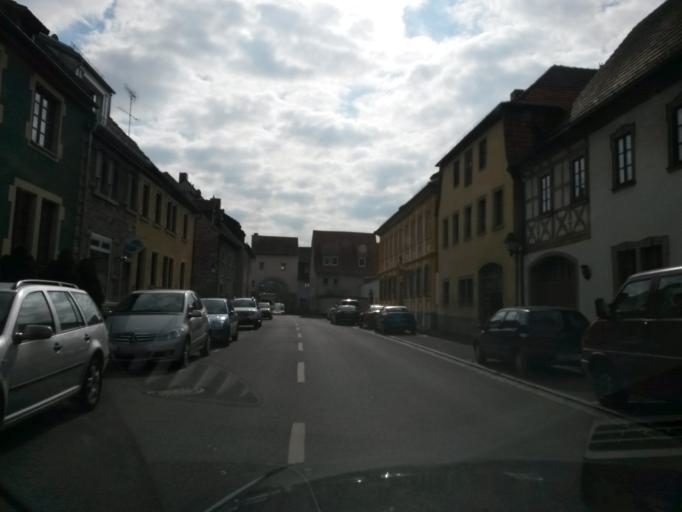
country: DE
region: Bavaria
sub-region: Regierungsbezirk Unterfranken
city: Eibelstadt
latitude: 49.7231
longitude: 10.0021
